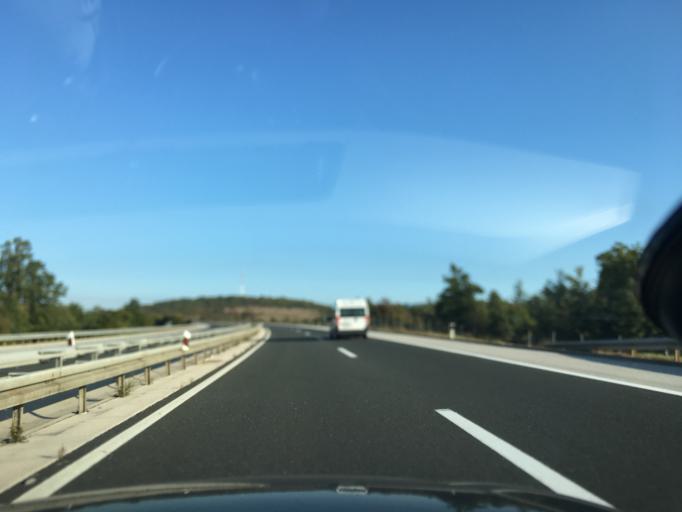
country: HR
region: Licko-Senjska
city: Gospic
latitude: 44.6479
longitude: 15.4345
